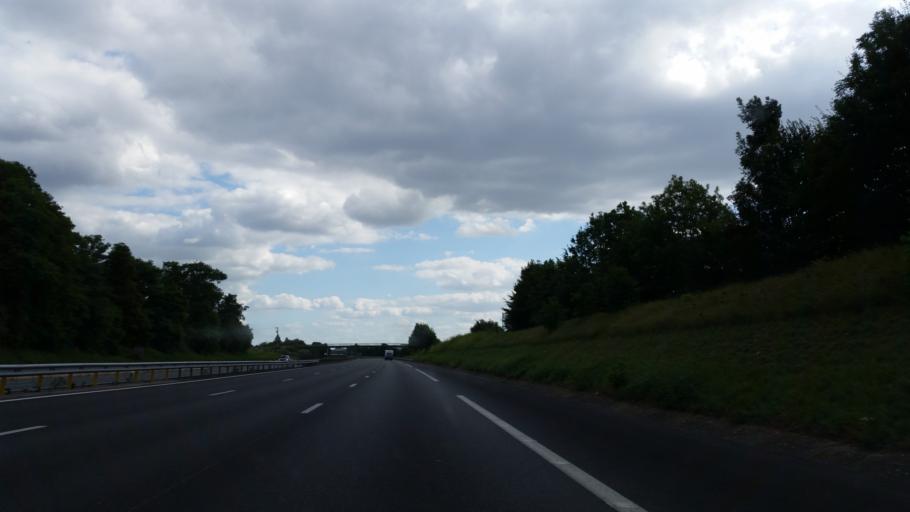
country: FR
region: Nord-Pas-de-Calais
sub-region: Departement du Pas-de-Calais
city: Bapaume
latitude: 50.0812
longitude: 2.8699
